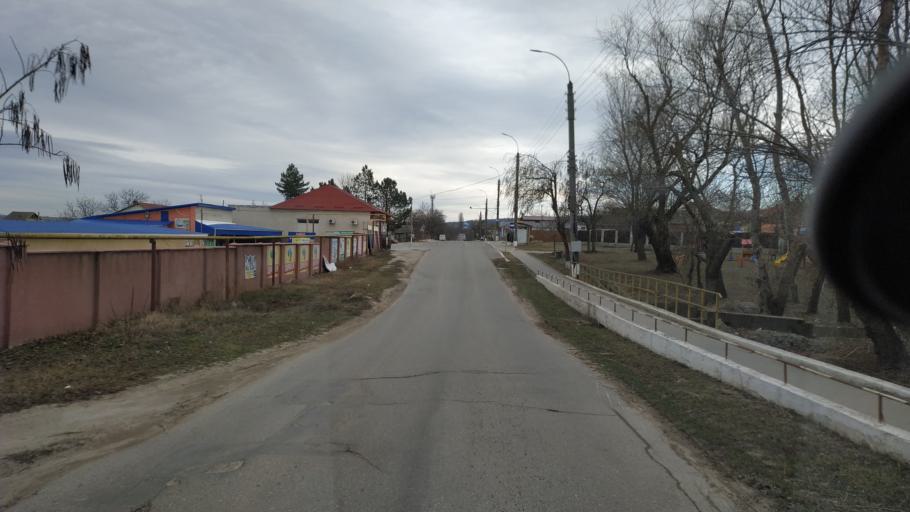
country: MD
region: Chisinau
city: Vadul lui Voda
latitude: 47.0942
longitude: 29.0730
